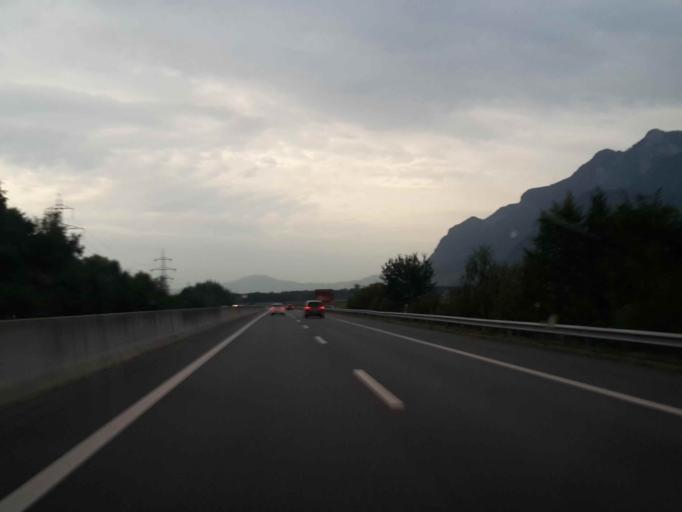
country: CH
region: Vaud
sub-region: Aigle District
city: Aigle
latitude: 46.3000
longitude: 6.9561
